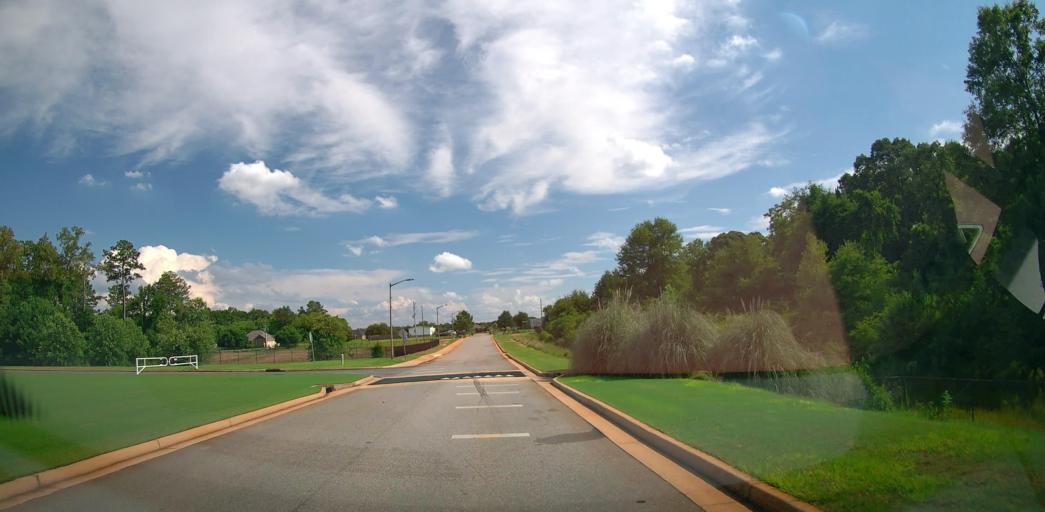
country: US
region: Georgia
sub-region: Houston County
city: Centerville
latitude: 32.5398
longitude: -83.6782
